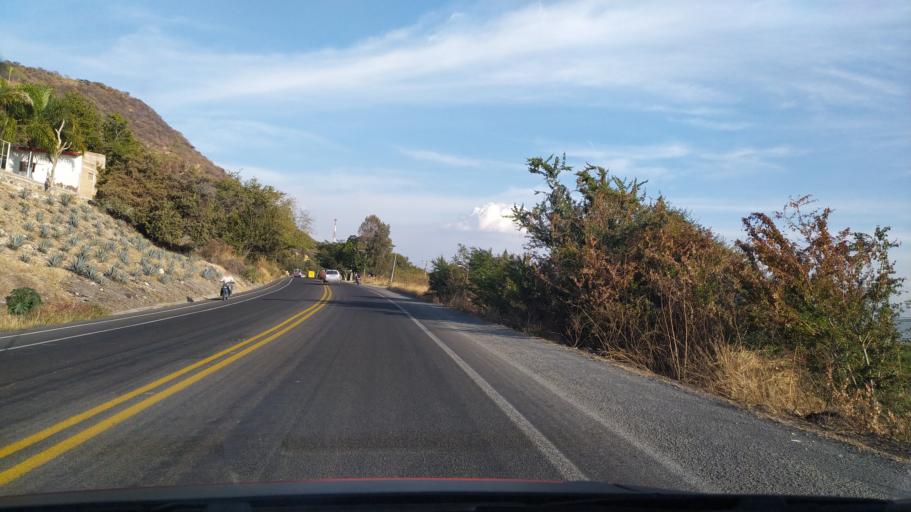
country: MX
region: Jalisco
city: Jamay
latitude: 20.2940
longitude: -102.7512
